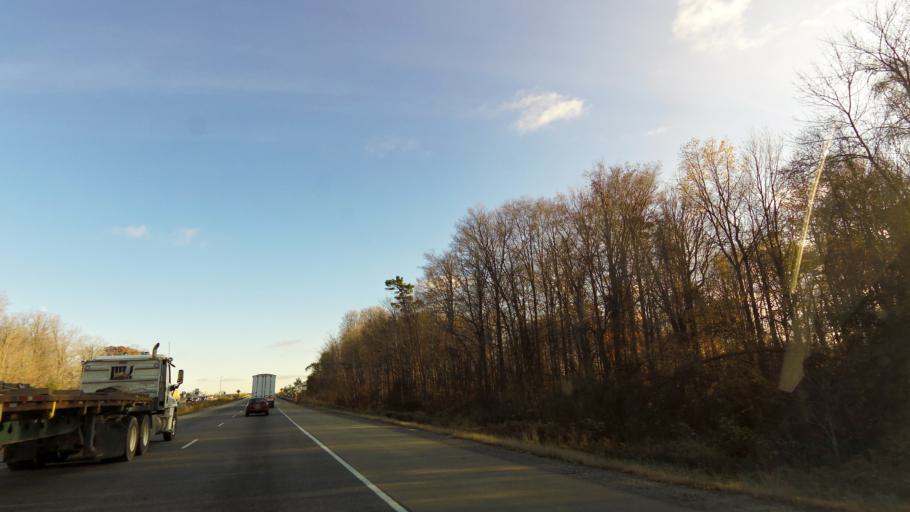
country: CA
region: Ontario
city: Cambridge
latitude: 43.4060
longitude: -80.3828
